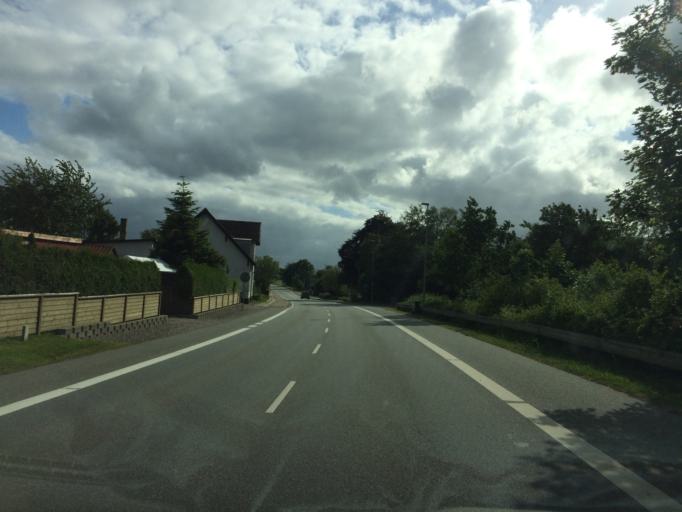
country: DK
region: South Denmark
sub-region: Sonderborg Kommune
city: Augustenborg
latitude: 54.9664
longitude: 9.9273
